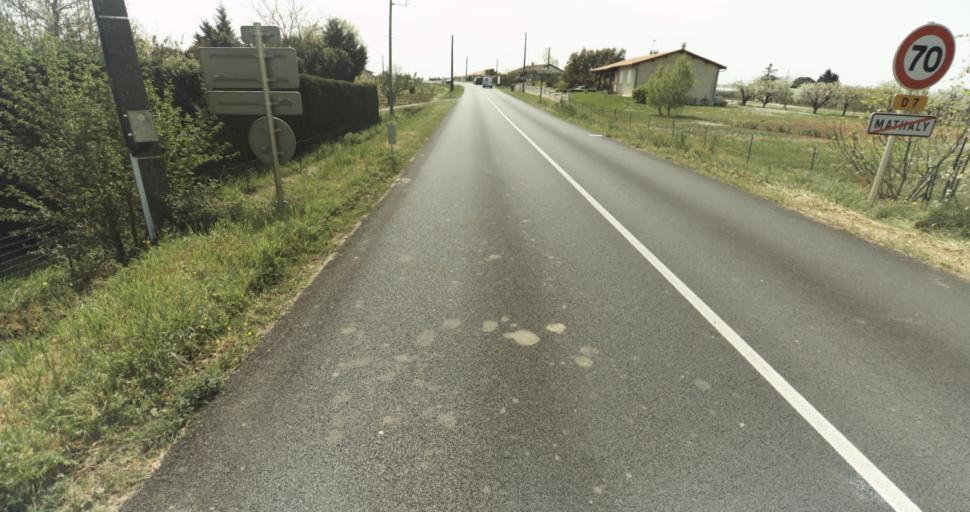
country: FR
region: Midi-Pyrenees
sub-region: Departement du Tarn-et-Garonne
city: Moissac
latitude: 44.1292
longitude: 1.0683
